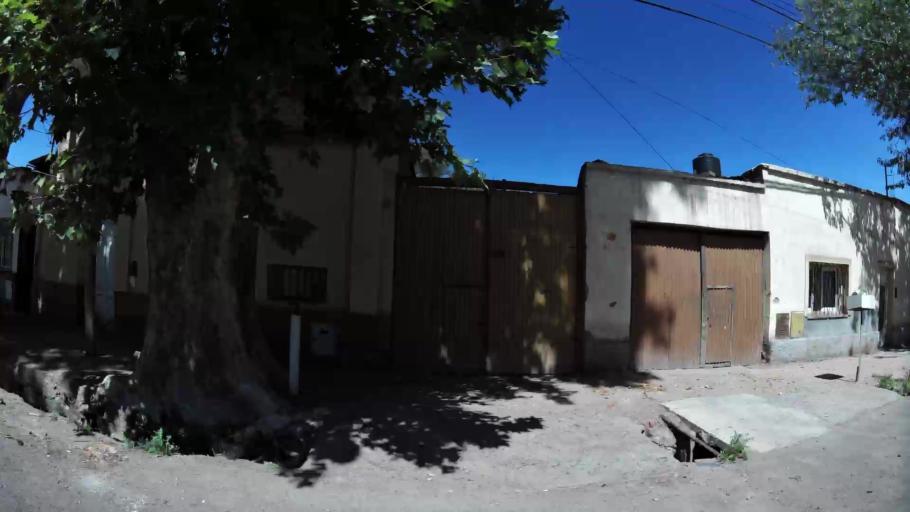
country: AR
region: Mendoza
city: Villa Nueva
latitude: -32.8675
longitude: -68.7879
